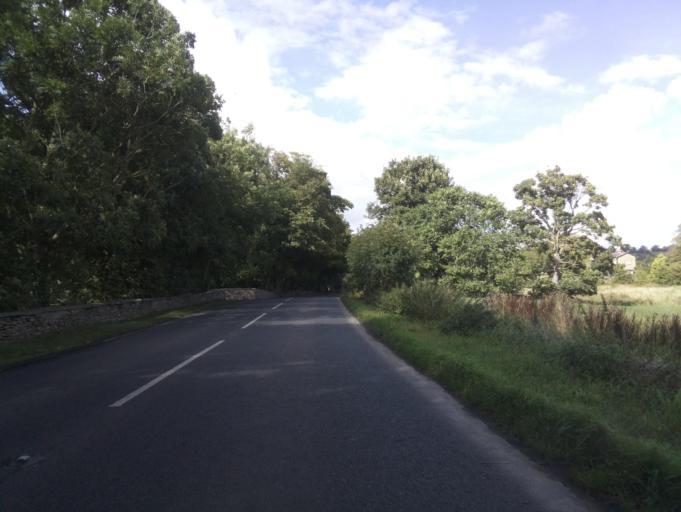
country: GB
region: England
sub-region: North Yorkshire
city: Leyburn
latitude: 54.3282
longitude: -1.8253
